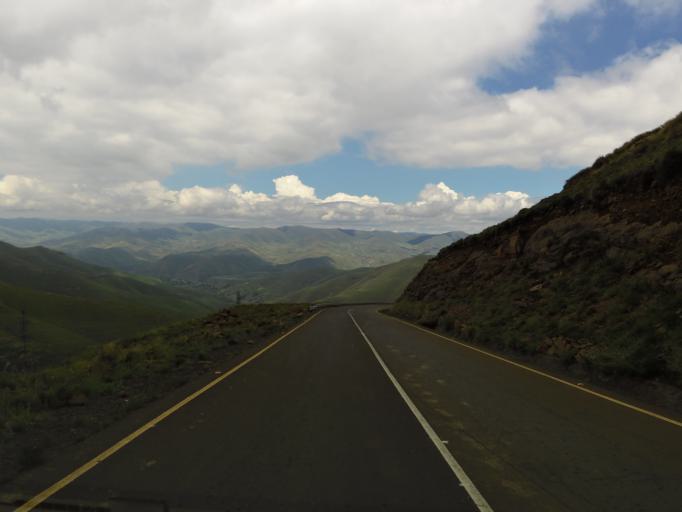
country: LS
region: Butha-Buthe
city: Butha-Buthe
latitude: -29.1058
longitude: 28.4317
